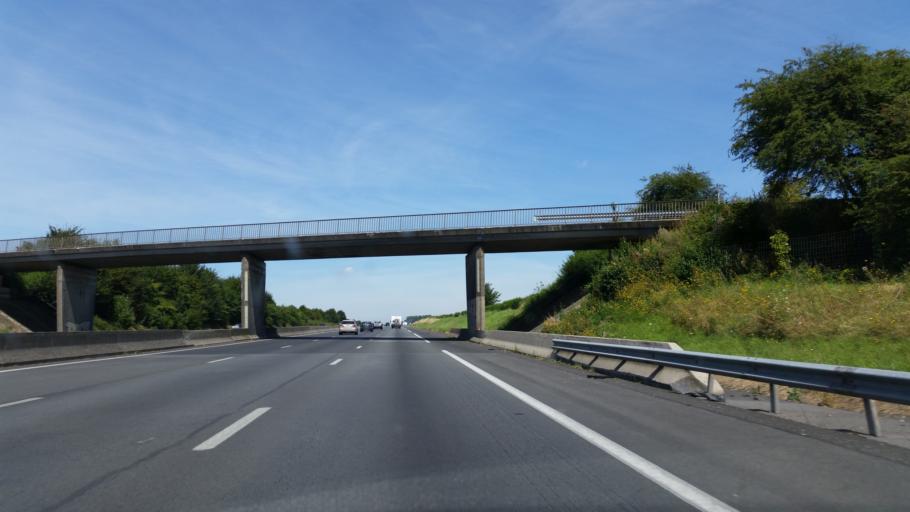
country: FR
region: Nord-Pas-de-Calais
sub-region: Departement du Pas-de-Calais
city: Vaulx-Vraucourt
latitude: 50.1370
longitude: 2.8721
